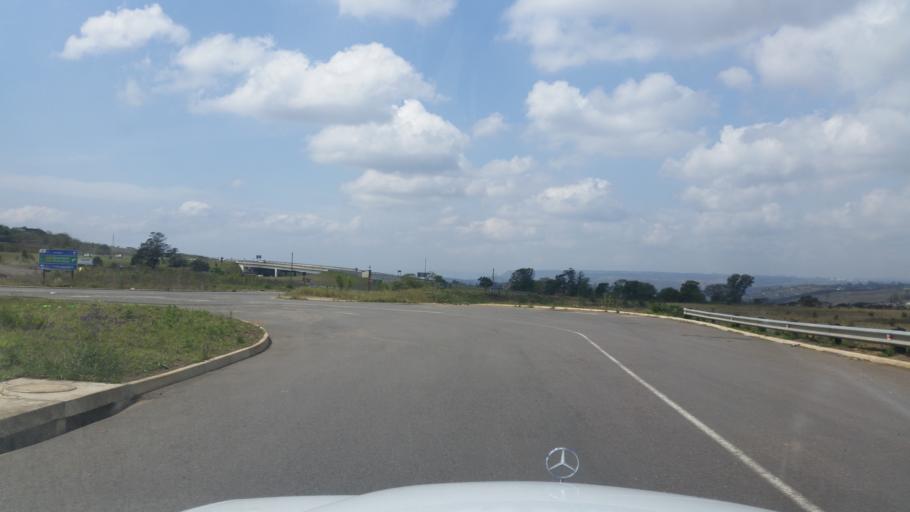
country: ZA
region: KwaZulu-Natal
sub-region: uMgungundlovu District Municipality
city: Camperdown
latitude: -29.7213
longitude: 30.4949
